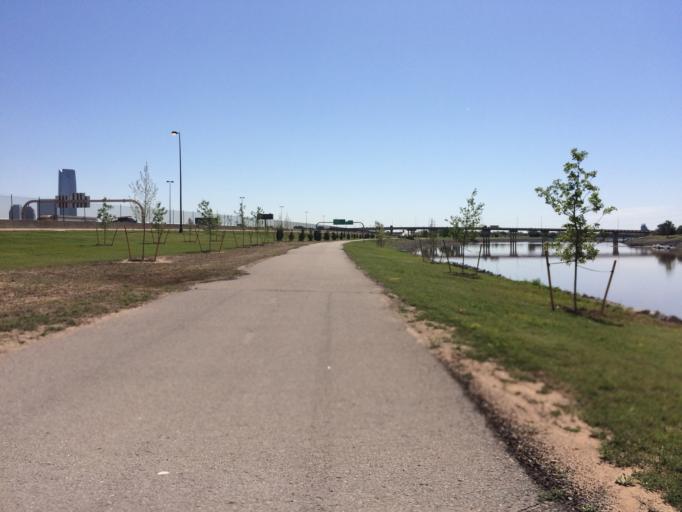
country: US
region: Oklahoma
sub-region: Oklahoma County
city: Oklahoma City
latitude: 35.4608
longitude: -97.5436
